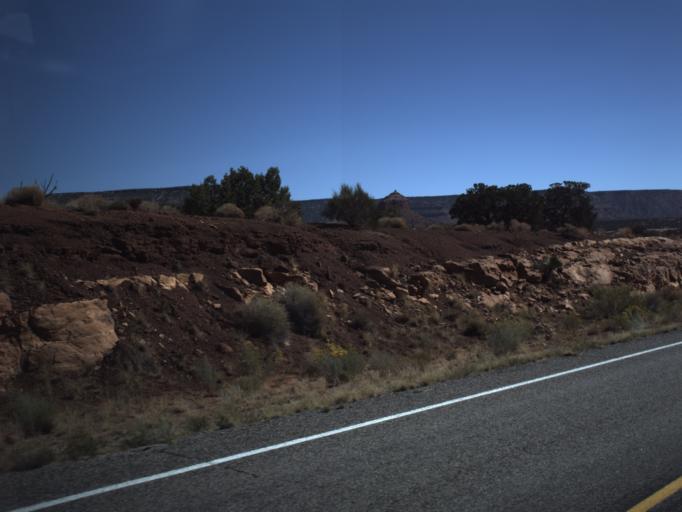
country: US
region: Utah
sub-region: San Juan County
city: Blanding
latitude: 37.6504
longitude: -110.1207
